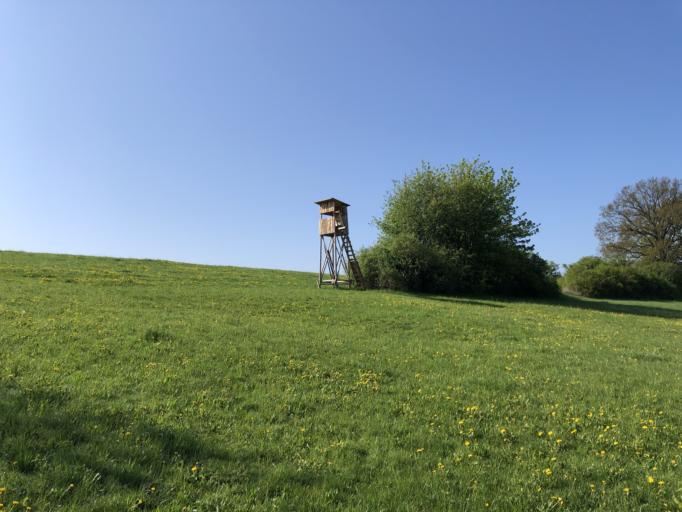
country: DE
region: Baden-Wuerttemberg
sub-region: Tuebingen Region
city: Tuebingen
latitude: 48.5498
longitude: 9.0453
